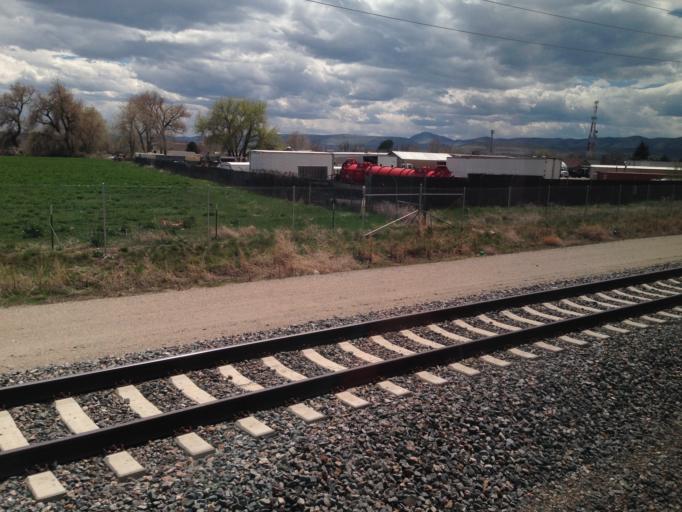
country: US
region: Colorado
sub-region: Jefferson County
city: Arvada
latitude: 39.7889
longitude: -105.1284
